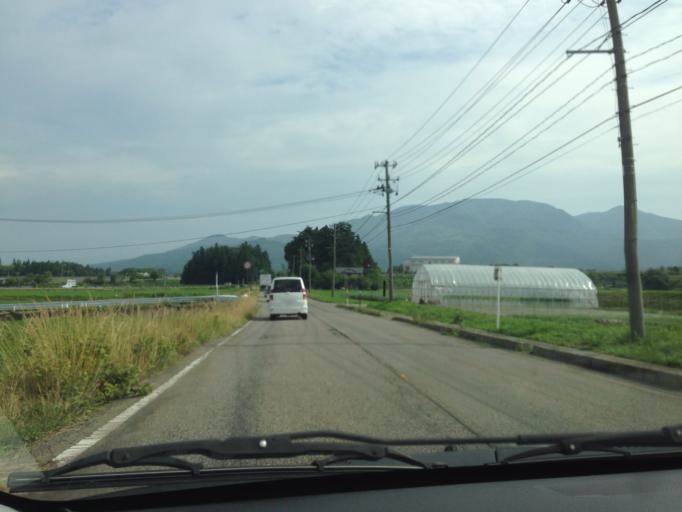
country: JP
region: Fukushima
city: Inawashiro
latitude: 37.5463
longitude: 139.9721
